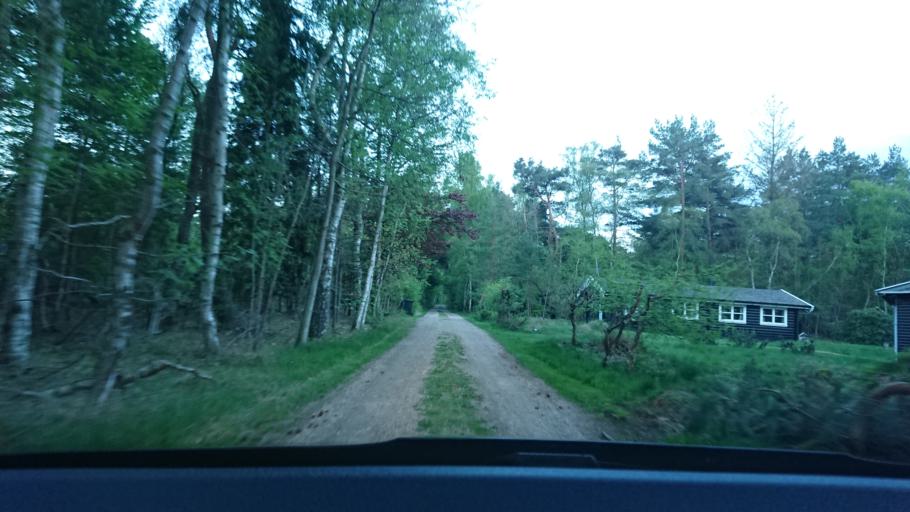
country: DK
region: Zealand
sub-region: Odsherred Kommune
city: Nykobing Sjaelland
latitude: 55.9417
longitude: 11.6981
